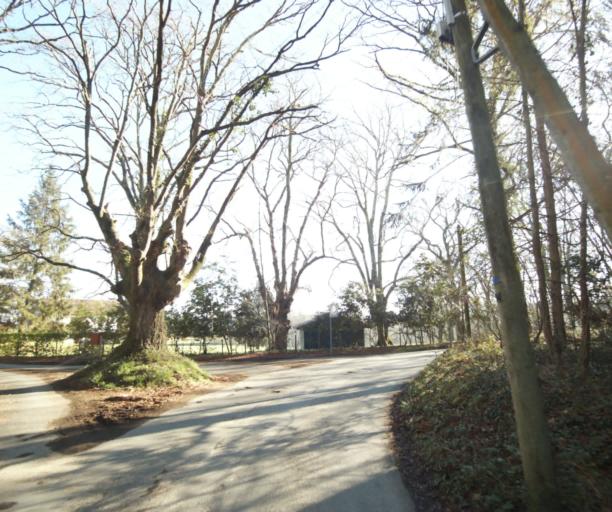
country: FR
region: Aquitaine
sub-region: Departement des Pyrenees-Atlantiques
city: Ciboure
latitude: 43.3689
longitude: -1.6662
